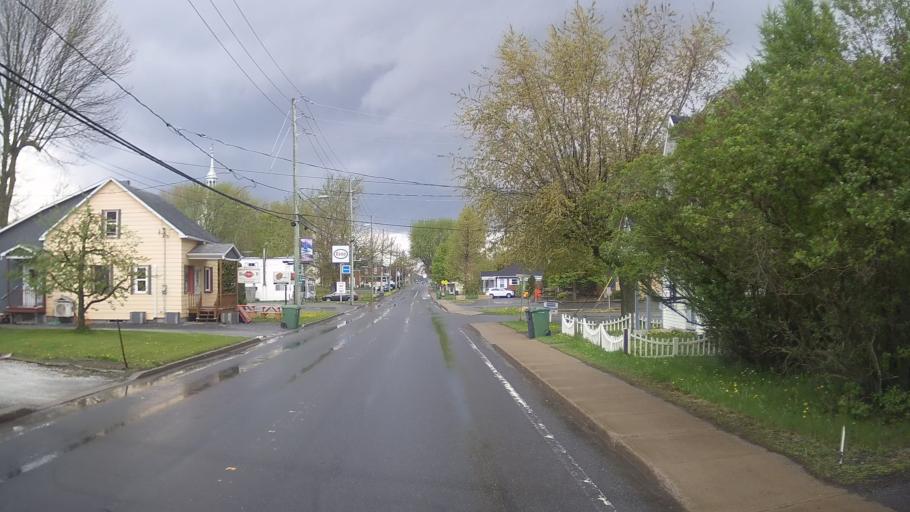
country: CA
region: Quebec
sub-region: Monteregie
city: Farnham
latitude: 45.3216
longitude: -73.0627
